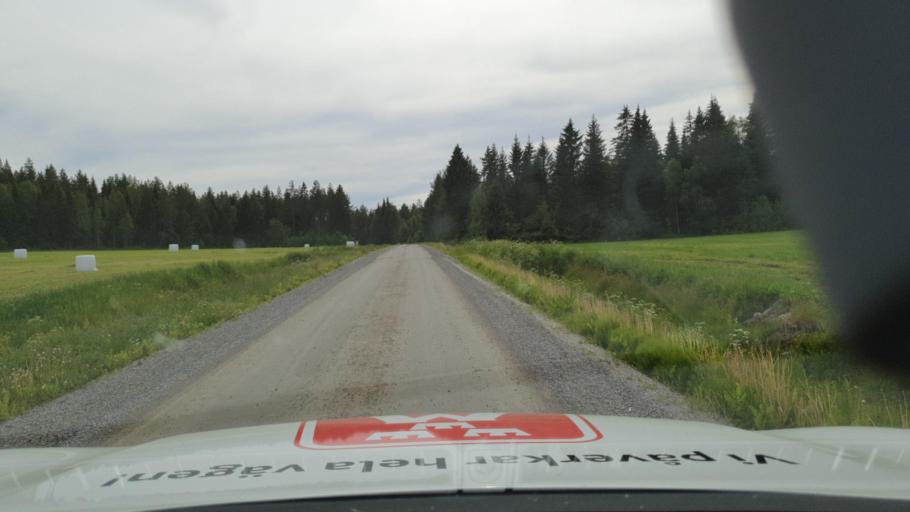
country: SE
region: Vaesterbotten
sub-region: Skelleftea Kommun
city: Burea
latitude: 64.4590
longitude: 21.0342
